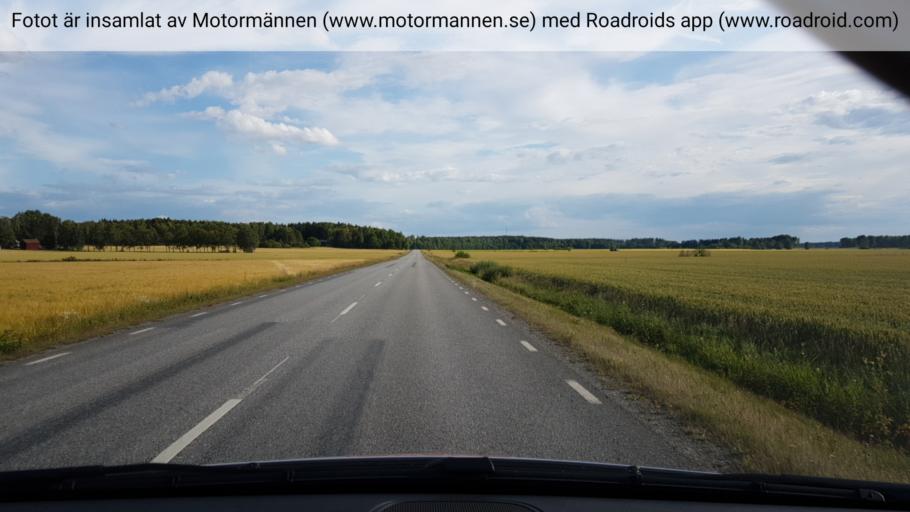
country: SE
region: Vaestmanland
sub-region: Vasteras
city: Skultuna
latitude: 59.7534
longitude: 16.4560
